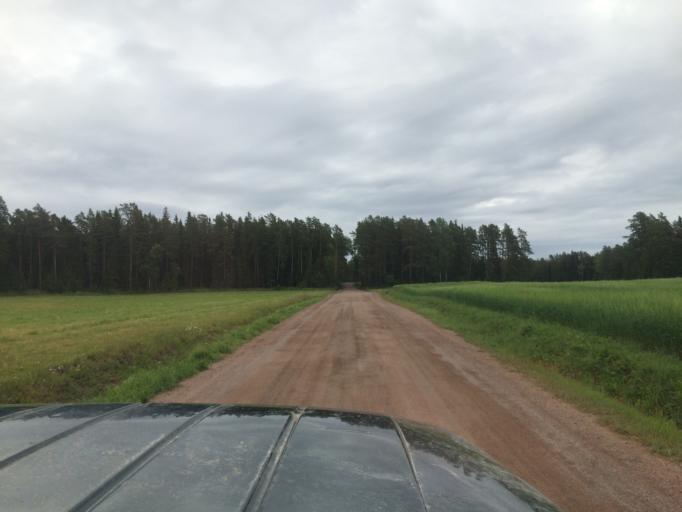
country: RU
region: Republic of Karelia
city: Sortavala
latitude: 61.3690
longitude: 30.9096
